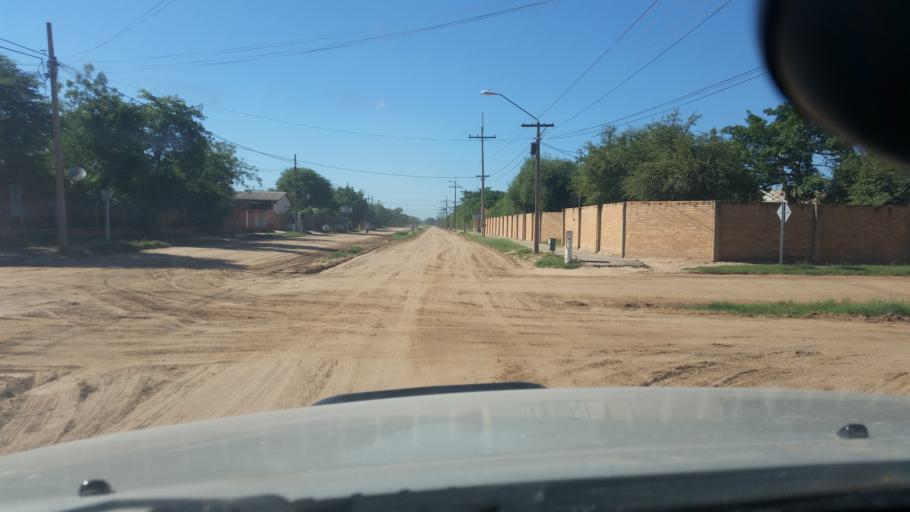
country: PY
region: Boqueron
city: Filadelfia
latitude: -22.3583
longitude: -60.0272
